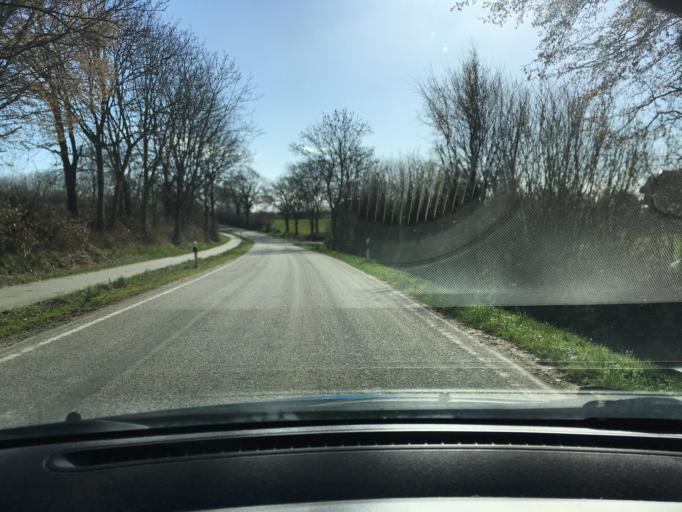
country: DE
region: Schleswig-Holstein
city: Fahrdorf
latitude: 54.5034
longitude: 9.6302
